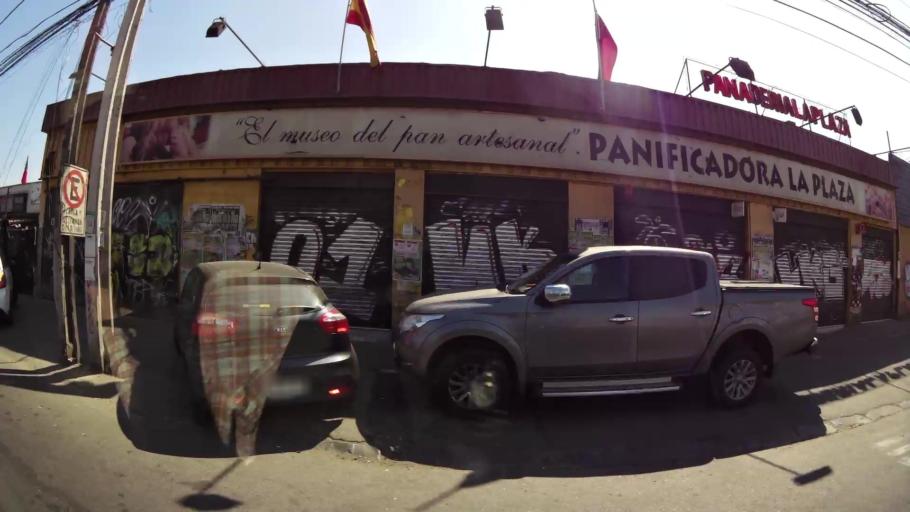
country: CL
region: Santiago Metropolitan
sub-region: Provincia de Santiago
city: Lo Prado
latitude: -33.4034
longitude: -70.7066
